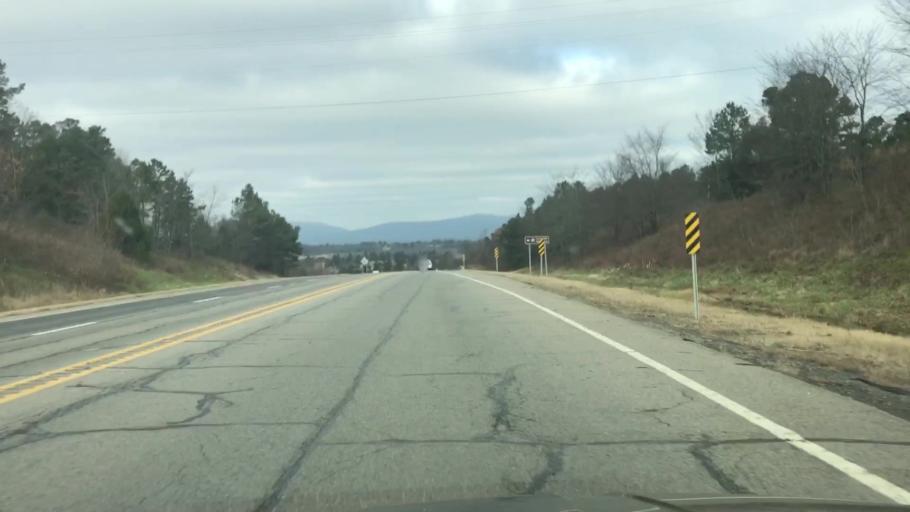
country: US
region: Arkansas
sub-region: Scott County
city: Waldron
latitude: 34.8634
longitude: -94.0730
